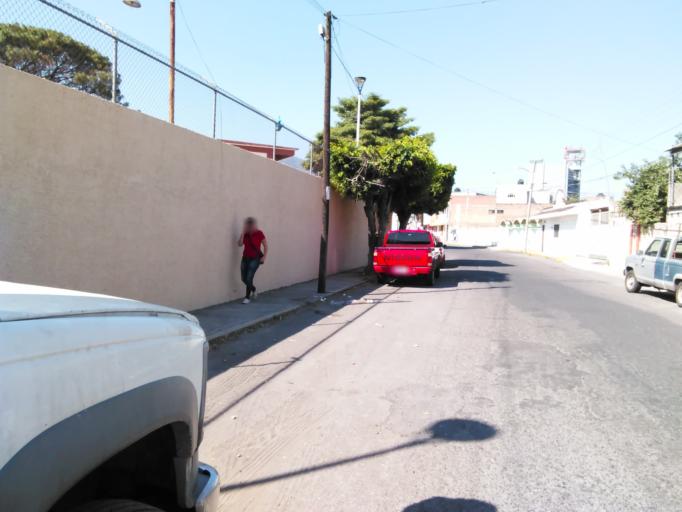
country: MX
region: Nayarit
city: Tepic
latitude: 21.4972
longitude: -104.8910
